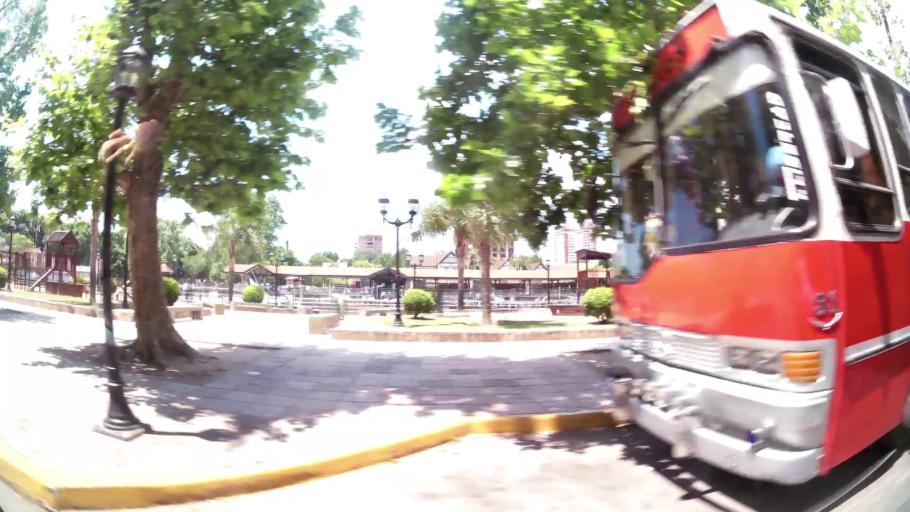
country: AR
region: Buenos Aires
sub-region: Partido de Tigre
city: Tigre
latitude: -34.4206
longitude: -58.5805
